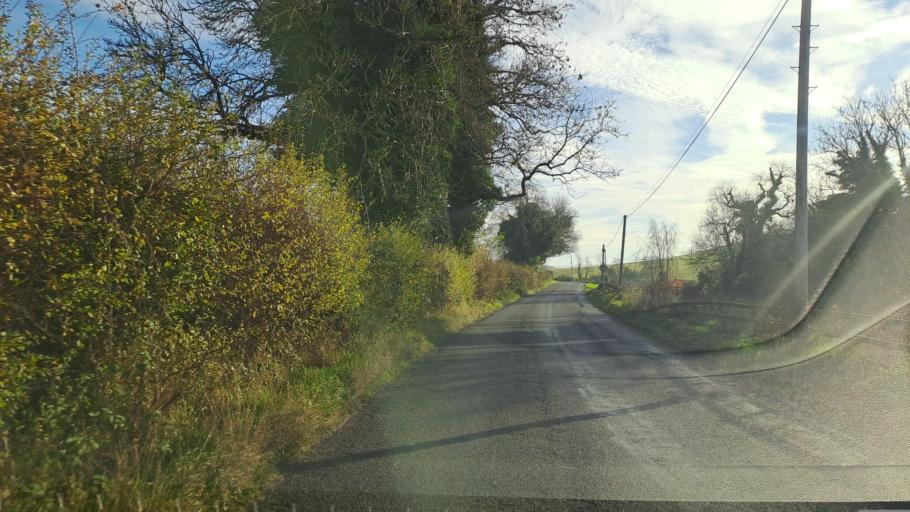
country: IE
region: Ulster
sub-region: County Monaghan
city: Carrickmacross
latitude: 53.8608
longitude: -6.6775
